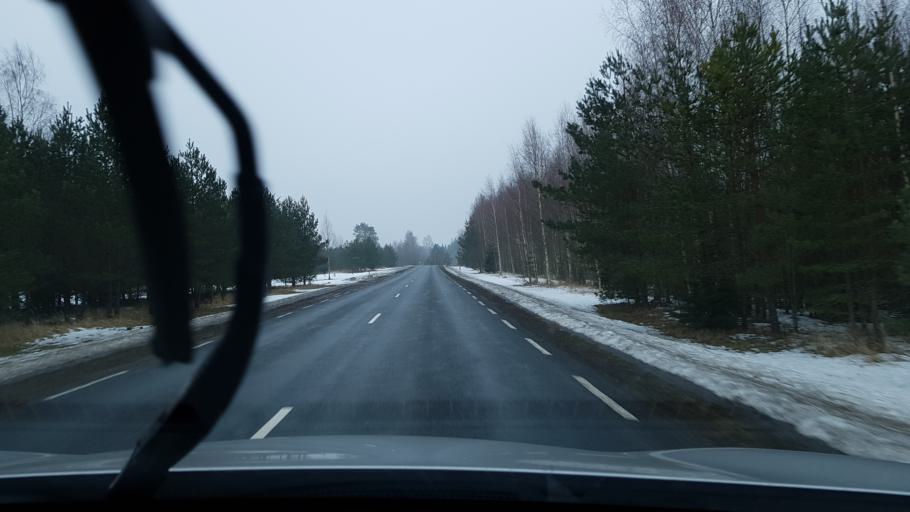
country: EE
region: Valgamaa
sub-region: Torva linn
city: Torva
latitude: 58.1246
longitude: 25.9925
